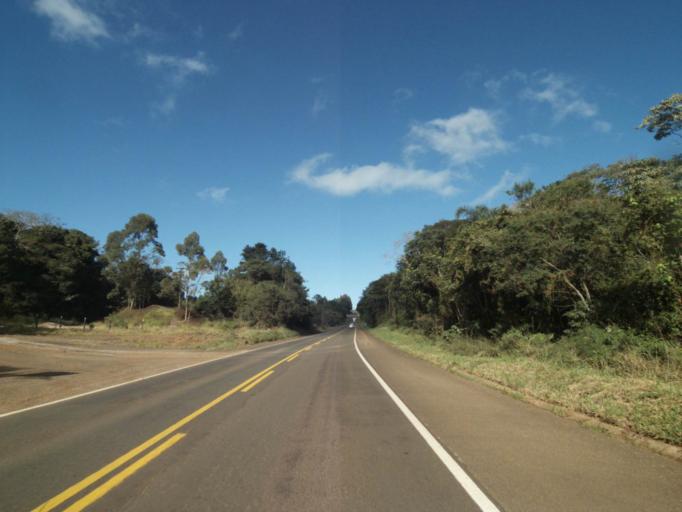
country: BR
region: Parana
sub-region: Faxinal
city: Faxinal
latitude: -23.8978
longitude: -51.1882
